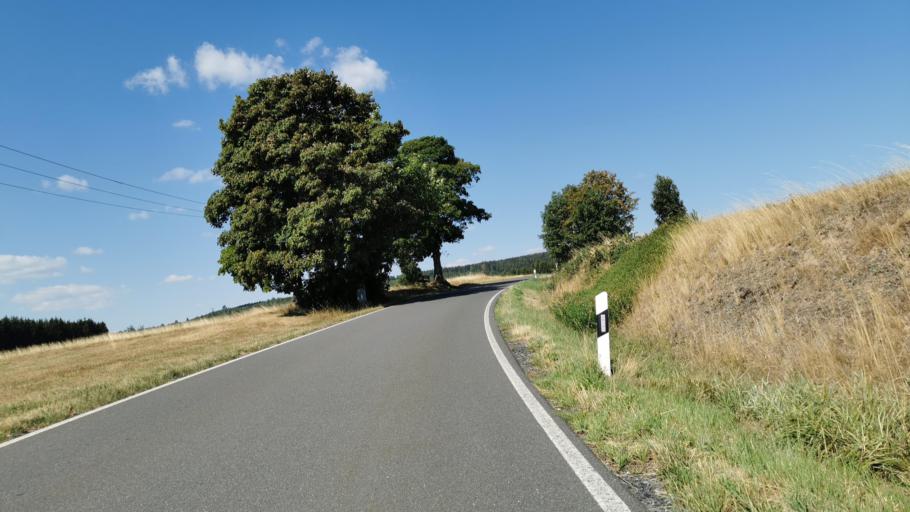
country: DE
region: Bavaria
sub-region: Upper Franconia
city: Tettau
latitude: 50.4341
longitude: 11.2799
